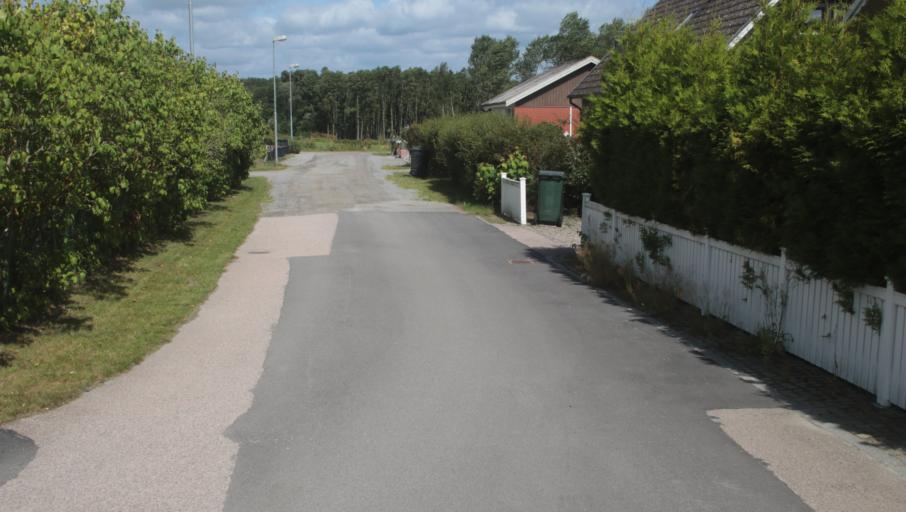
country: SE
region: Blekinge
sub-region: Karlshamns Kommun
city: Morrum
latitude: 56.1642
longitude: 14.6823
